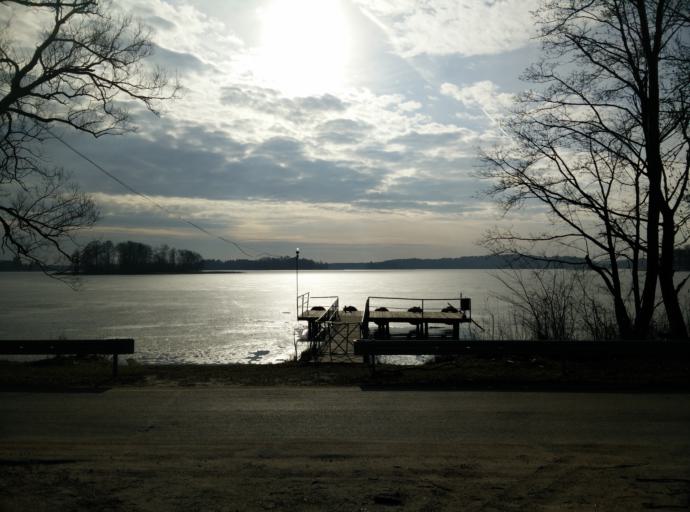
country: LT
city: Trakai
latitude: 54.6685
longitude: 24.9415
